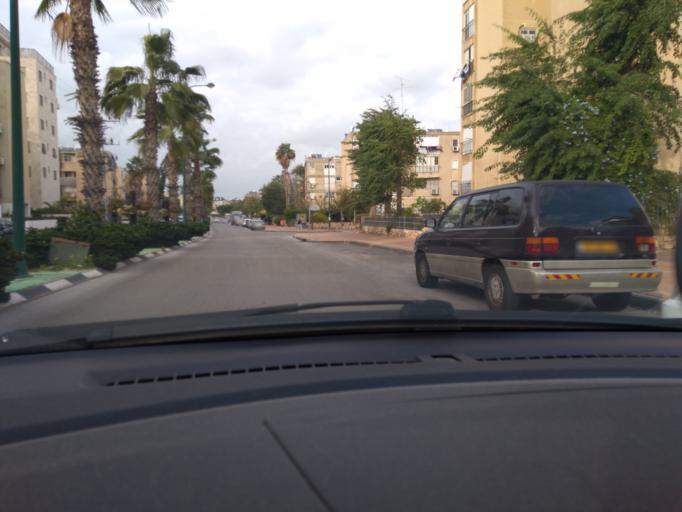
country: IL
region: Central District
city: Netanya
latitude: 32.3388
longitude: 34.8566
